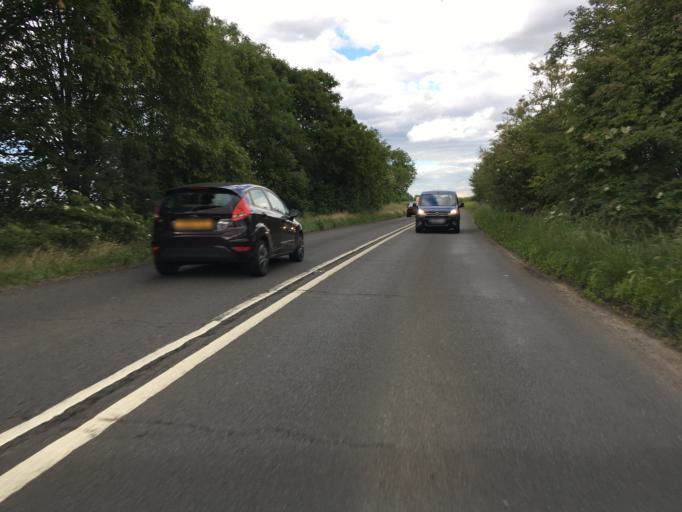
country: GB
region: England
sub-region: Buckinghamshire
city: Haddenham
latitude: 51.7725
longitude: -0.9560
